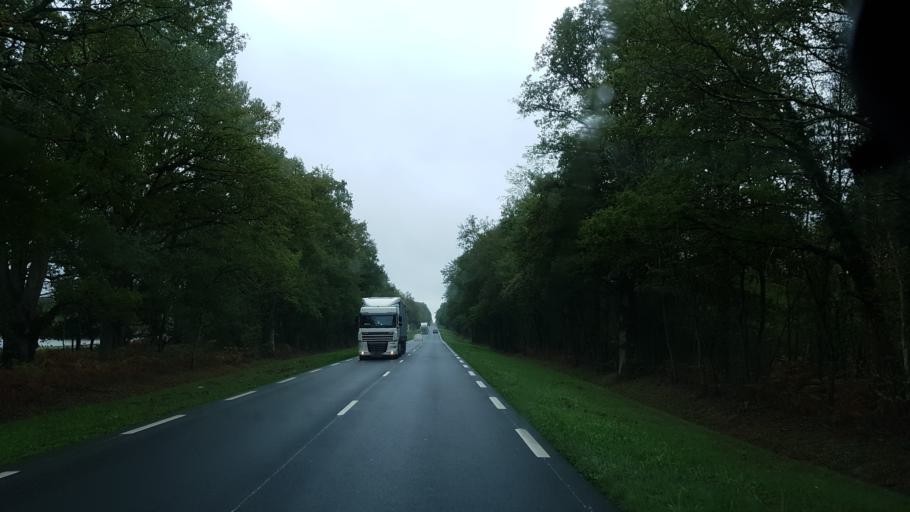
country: FR
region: Centre
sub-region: Departement du Loir-et-Cher
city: Salbris
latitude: 47.3950
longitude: 2.0547
